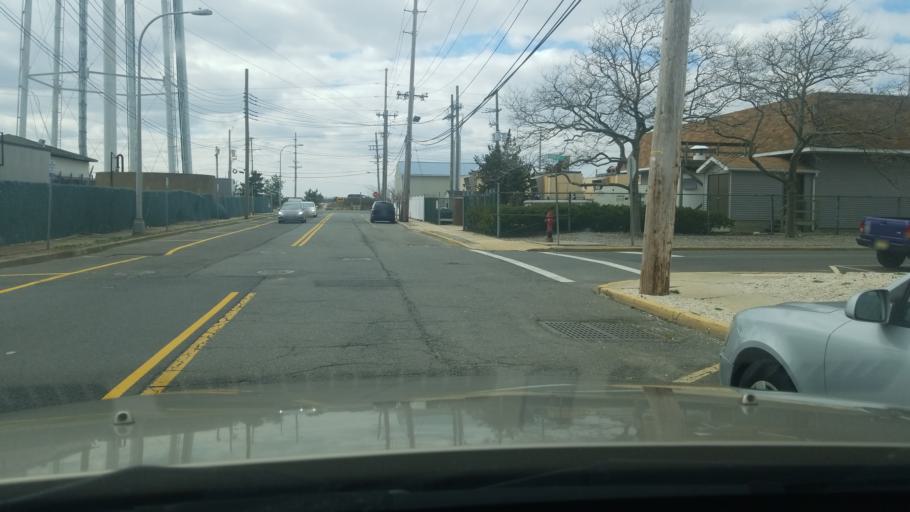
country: US
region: New Jersey
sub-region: Ocean County
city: Seaside Heights
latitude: 39.9438
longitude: -74.0776
